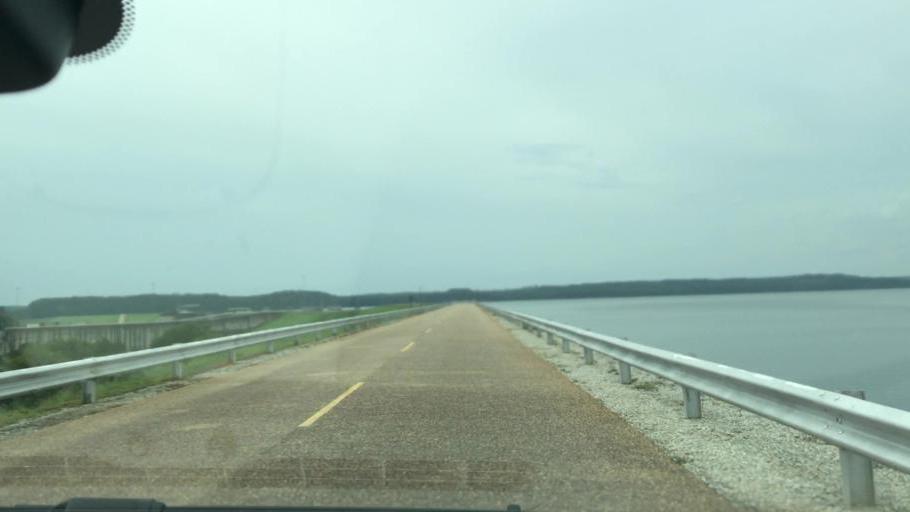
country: US
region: Georgia
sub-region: Clay County
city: Fort Gaines
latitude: 31.6291
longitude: -85.0571
